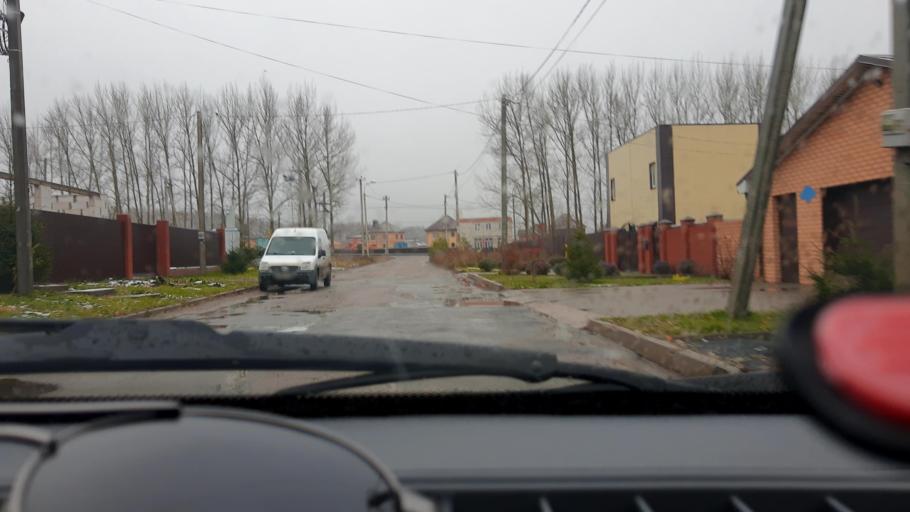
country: RU
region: Bashkortostan
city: Kabakovo
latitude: 54.6200
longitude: 56.1213
